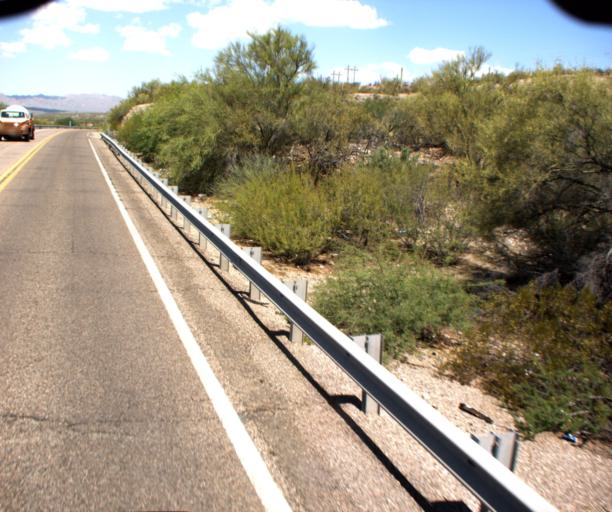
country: US
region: Arizona
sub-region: Pinal County
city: Kearny
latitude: 33.0113
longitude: -110.8218
